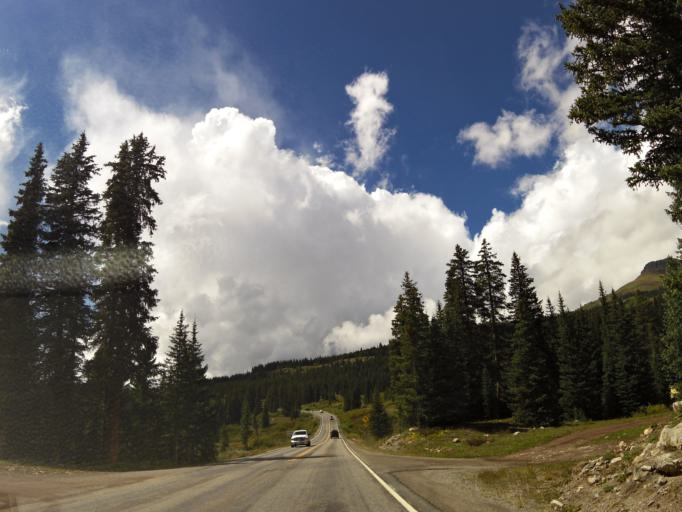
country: US
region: Colorado
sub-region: San Juan County
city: Silverton
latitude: 37.7482
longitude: -107.6887
